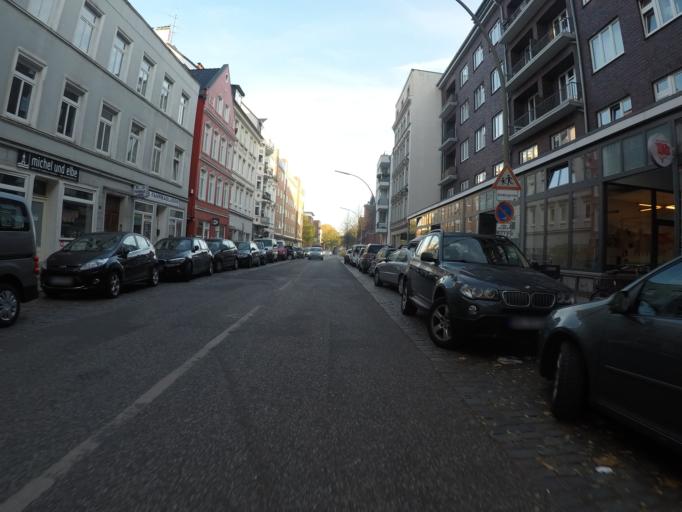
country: DE
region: Hamburg
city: St. Pauli
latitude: 53.5684
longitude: 9.9564
